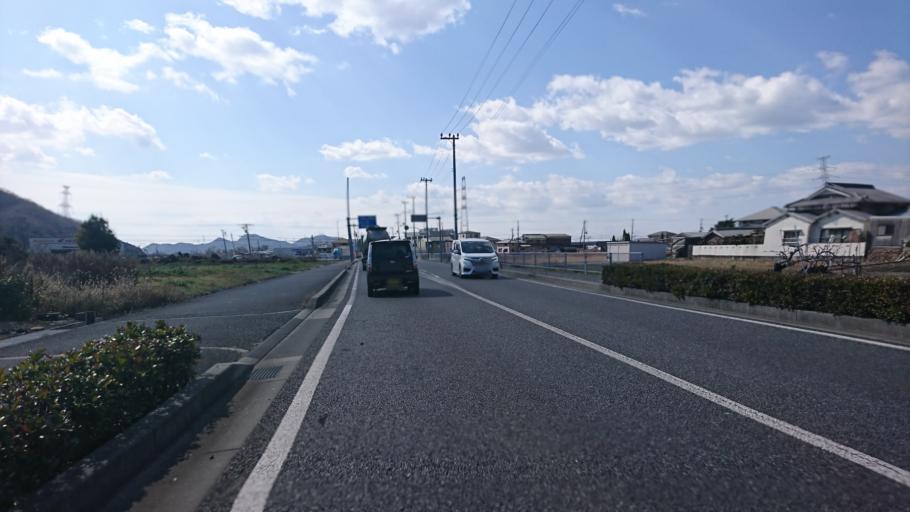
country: JP
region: Hyogo
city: Himeji
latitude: 34.8413
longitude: 134.7443
